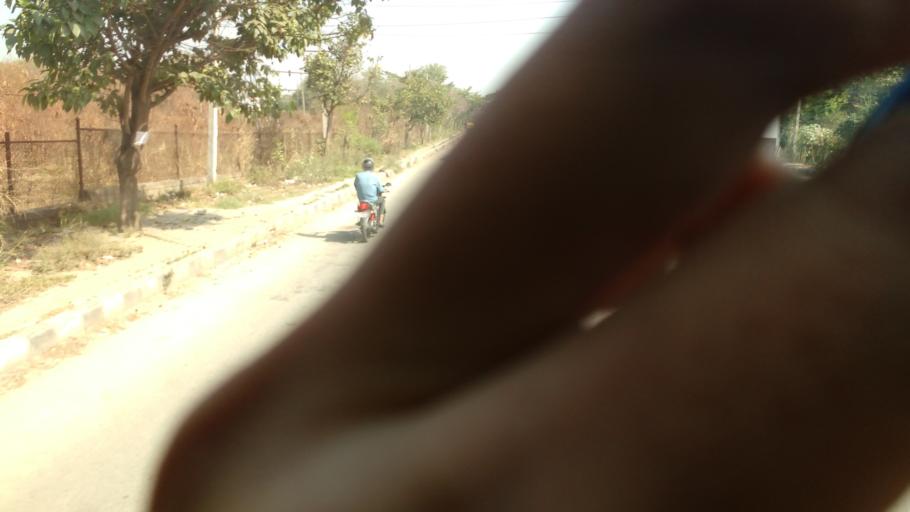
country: IN
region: Karnataka
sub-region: Bangalore Urban
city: Bangalore
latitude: 12.9444
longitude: 77.6389
